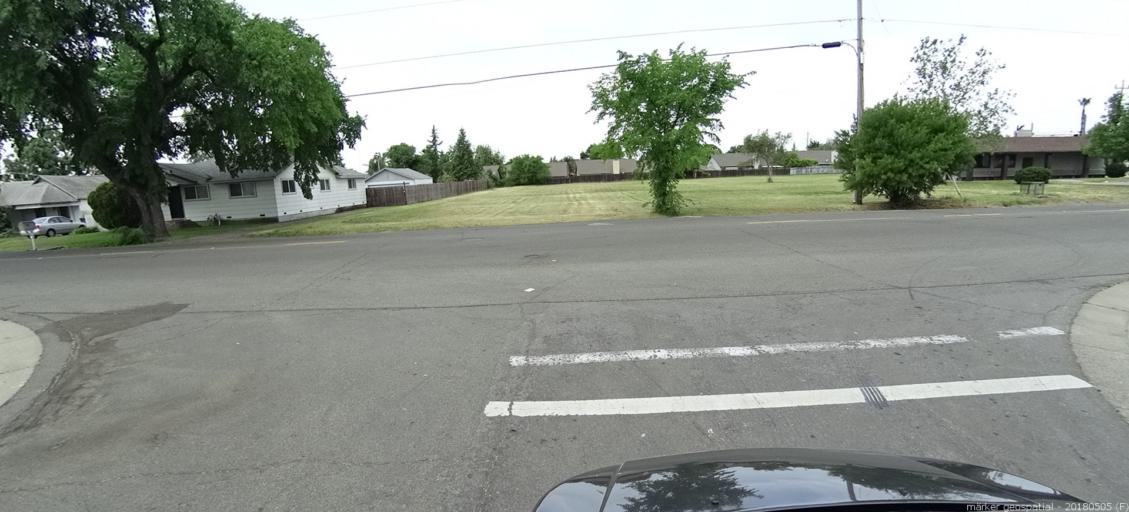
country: US
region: California
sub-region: Sacramento County
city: Rio Linda
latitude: 38.6468
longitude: -121.4381
